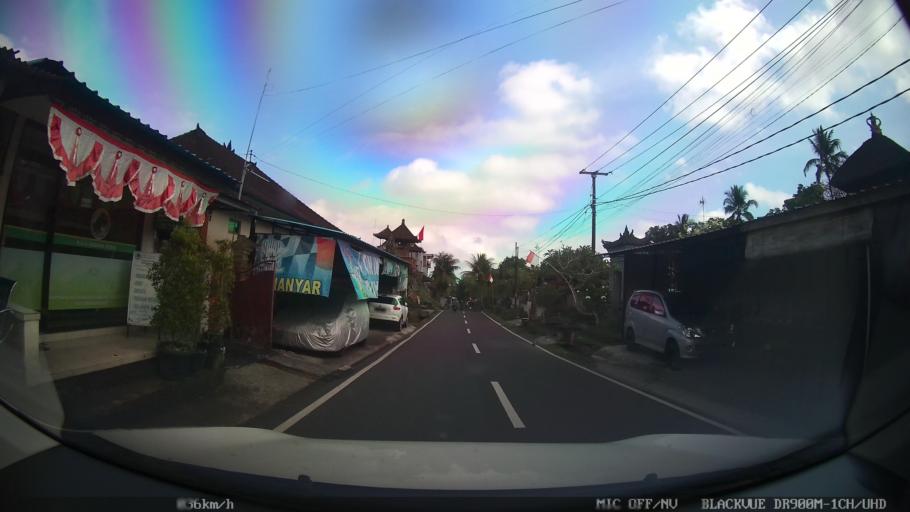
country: ID
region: Bali
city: Banjar Pesalakan
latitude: -8.4933
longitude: 115.2977
